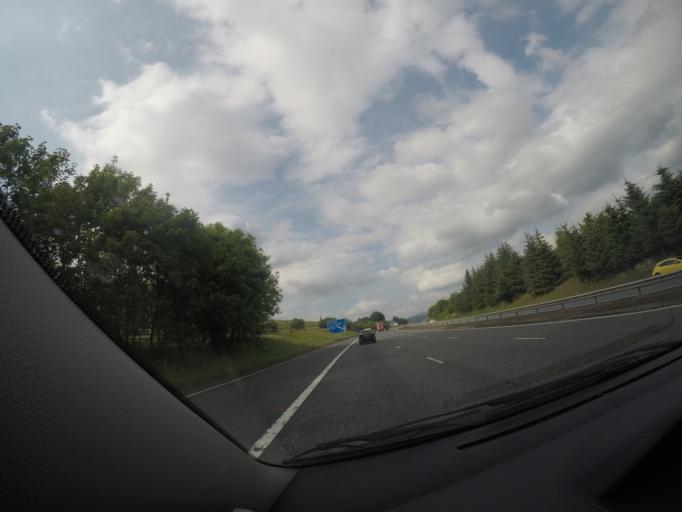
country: GB
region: Scotland
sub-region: South Lanarkshire
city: Douglas
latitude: 55.4918
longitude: -3.6963
